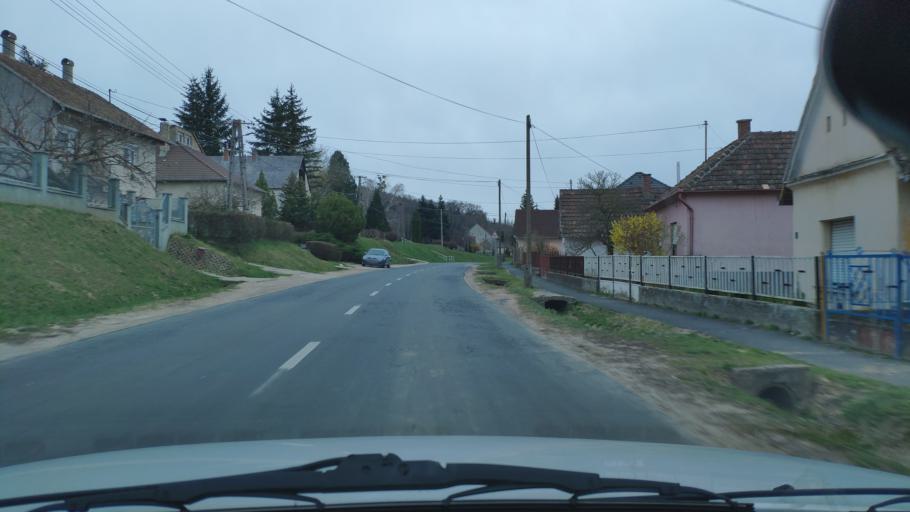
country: HU
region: Zala
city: Nagykanizsa
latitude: 46.5394
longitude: 16.9855
